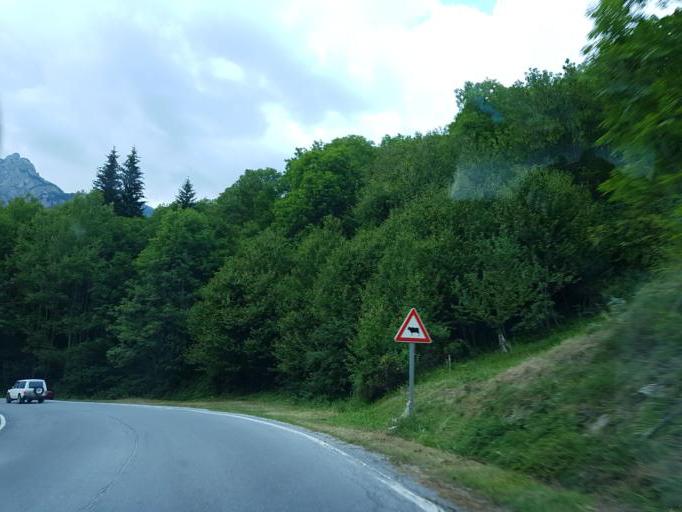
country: IT
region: Piedmont
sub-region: Provincia di Cuneo
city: Prazzo Superiore
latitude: 44.4764
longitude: 7.0399
